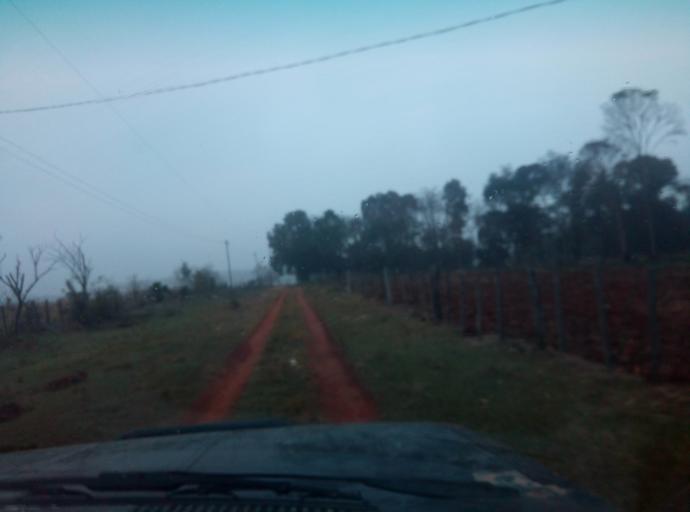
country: PY
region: Caaguazu
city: Doctor Cecilio Baez
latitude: -25.1576
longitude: -56.2615
